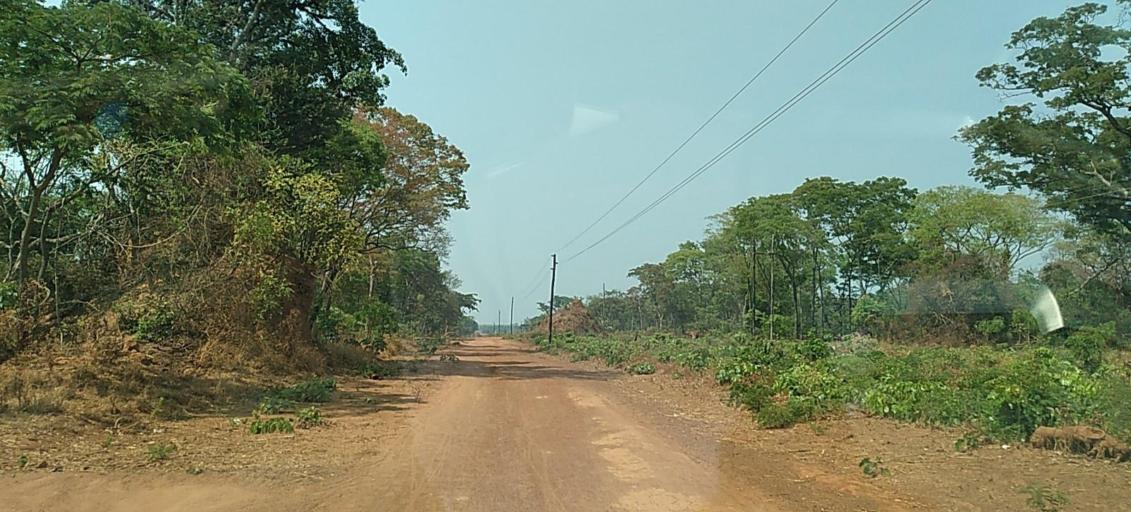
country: ZM
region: Copperbelt
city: Kalulushi
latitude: -13.0811
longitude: 27.4109
